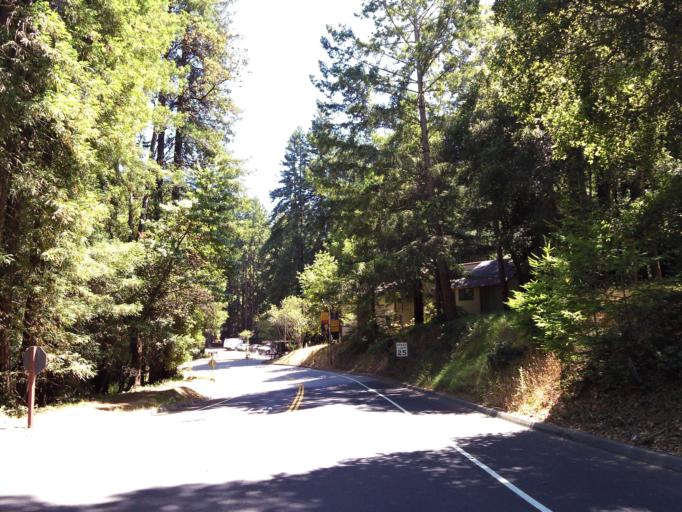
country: US
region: California
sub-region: Santa Cruz County
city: Pasatiempo
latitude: 36.9992
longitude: -122.0645
